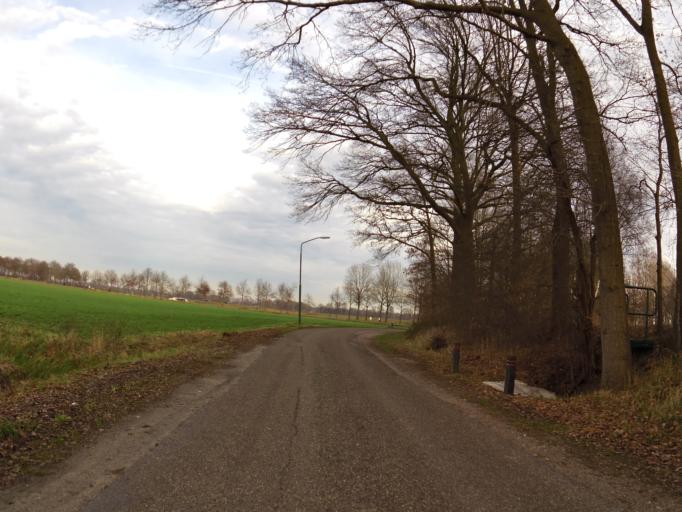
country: NL
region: North Brabant
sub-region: Gemeente Sint-Michielsgestel
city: Sint-Michielsgestel
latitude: 51.6592
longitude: 5.3384
